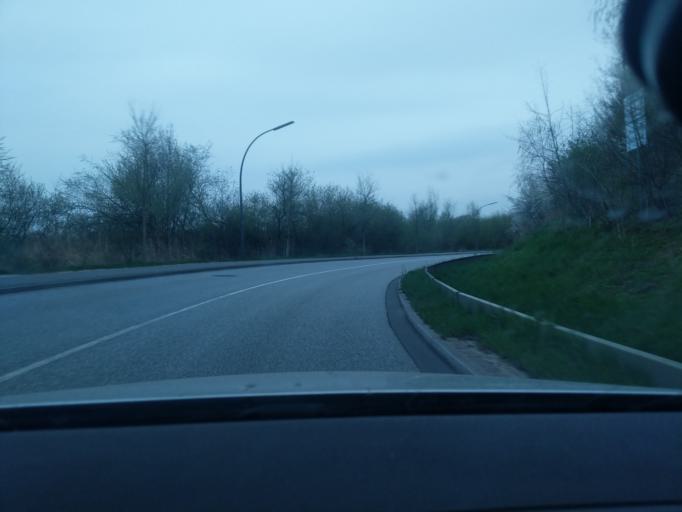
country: DE
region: Hamburg
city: Altona
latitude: 53.5149
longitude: 9.8809
